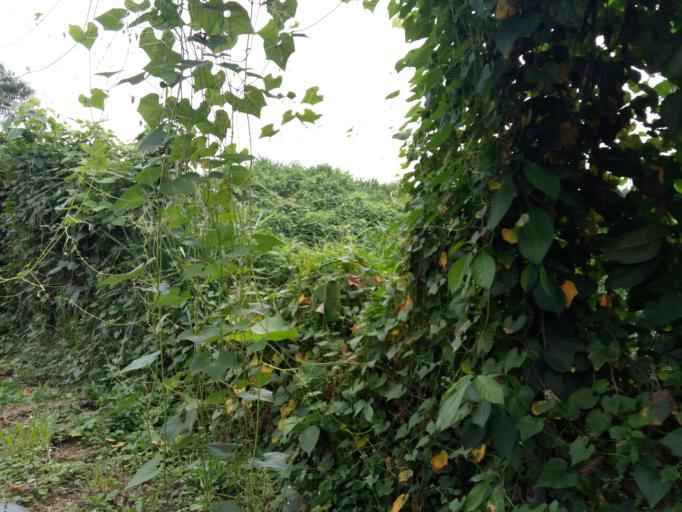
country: EC
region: Santo Domingo de los Tsachilas
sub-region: Canton Santo Domingo de los Colorados
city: Santo Domingo de los Colorados
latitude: -0.2297
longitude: -79.2061
